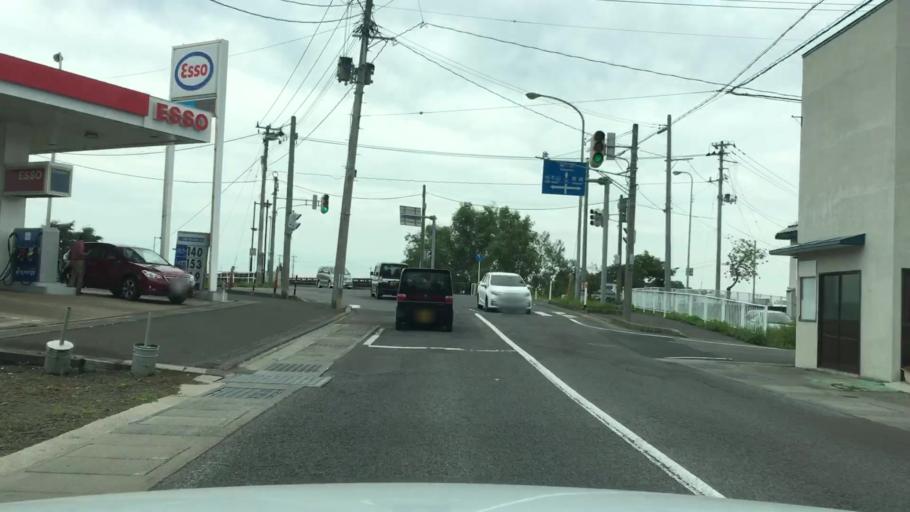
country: JP
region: Aomori
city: Hirosaki
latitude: 40.6144
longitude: 140.4621
